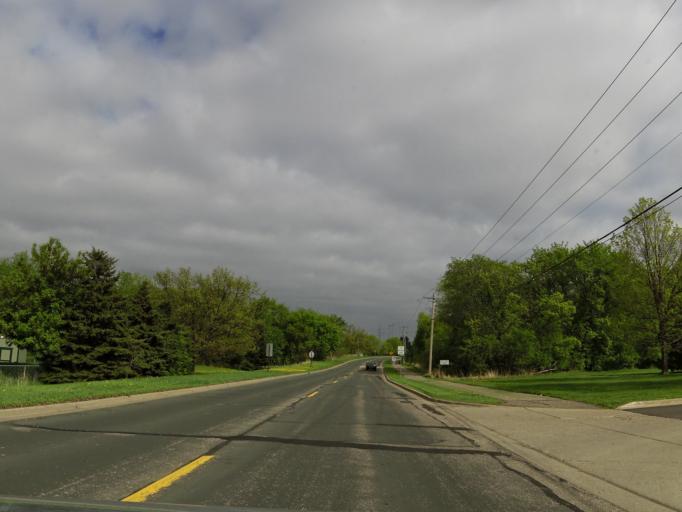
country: US
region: Minnesota
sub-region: Washington County
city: Woodbury
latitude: 44.9306
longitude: -92.9703
